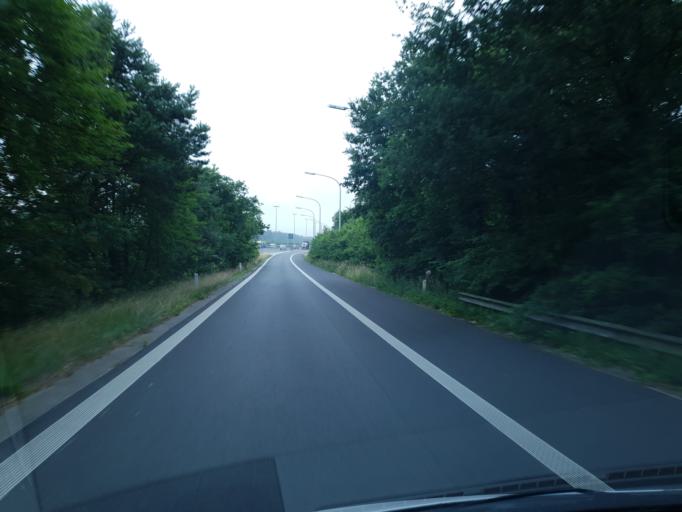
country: BE
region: Flanders
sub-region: Provincie Antwerpen
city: Brasschaat
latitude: 51.3100
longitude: 4.5607
